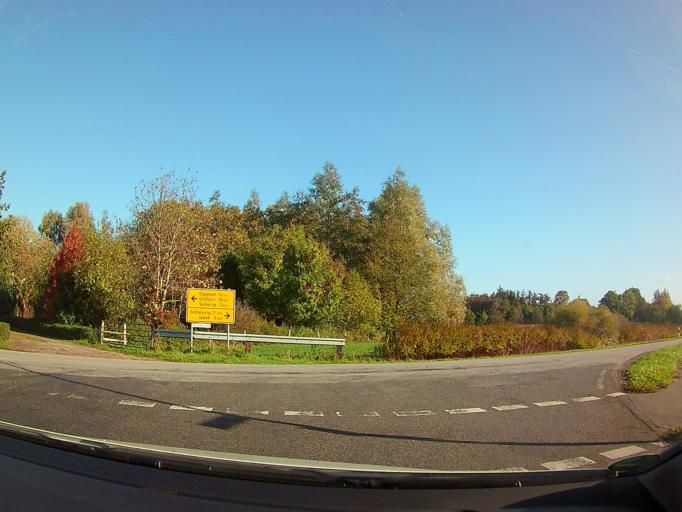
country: DE
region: Schleswig-Holstein
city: Sollerup
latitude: 54.5576
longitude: 9.3329
